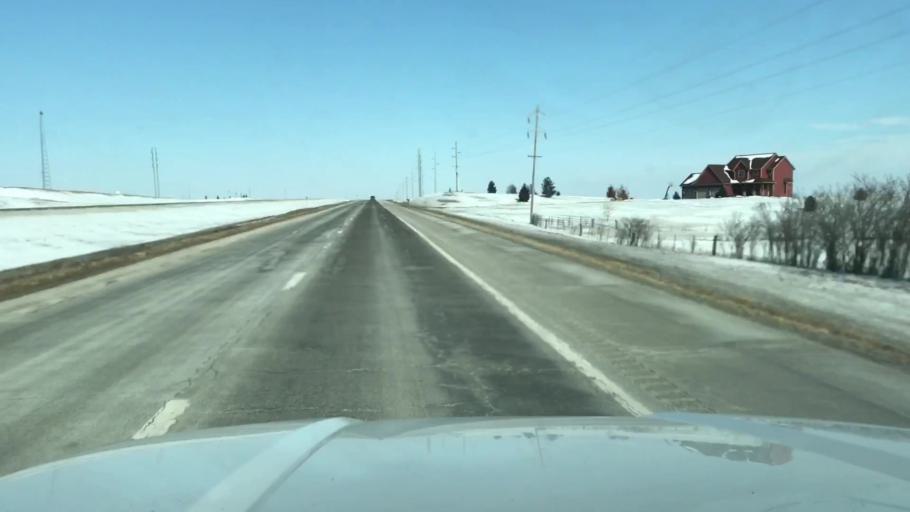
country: US
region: Missouri
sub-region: Nodaway County
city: Maryville
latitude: 40.2234
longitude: -94.8678
